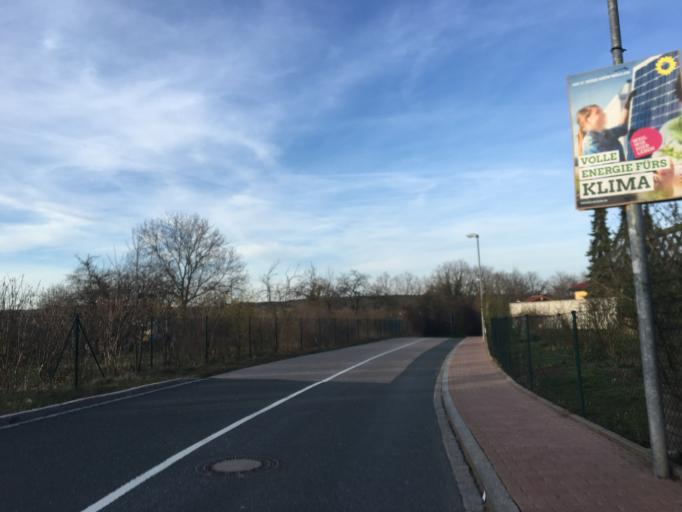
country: DE
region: Bavaria
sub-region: Regierungsbezirk Mittelfranken
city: Wilhermsdorf
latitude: 49.4767
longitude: 10.7208
